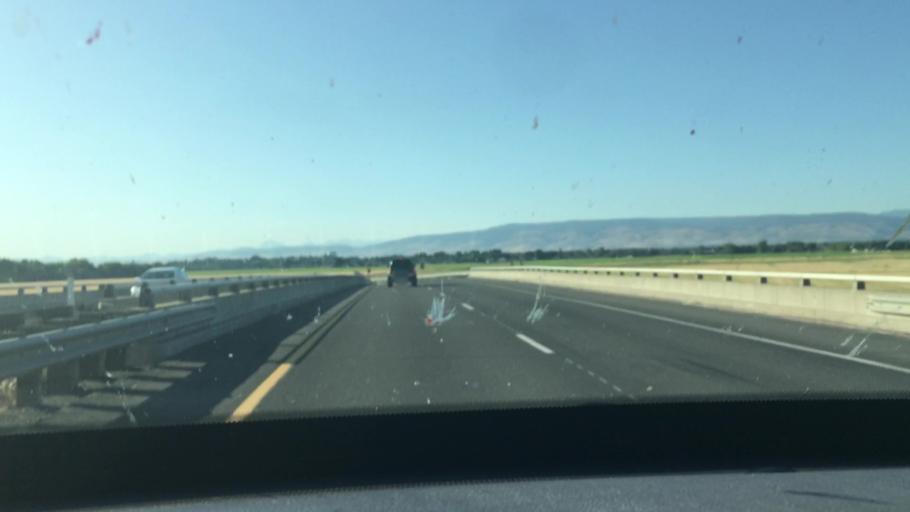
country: US
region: Washington
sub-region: Kittitas County
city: Ellensburg
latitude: 46.9713
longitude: -120.5102
